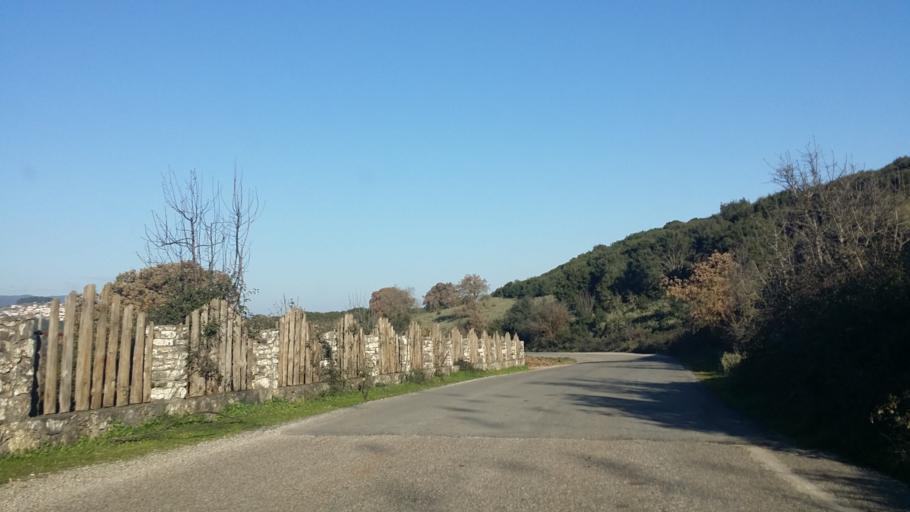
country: GR
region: West Greece
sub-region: Nomos Aitolias kai Akarnanias
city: Katouna
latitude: 38.7649
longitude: 21.1369
